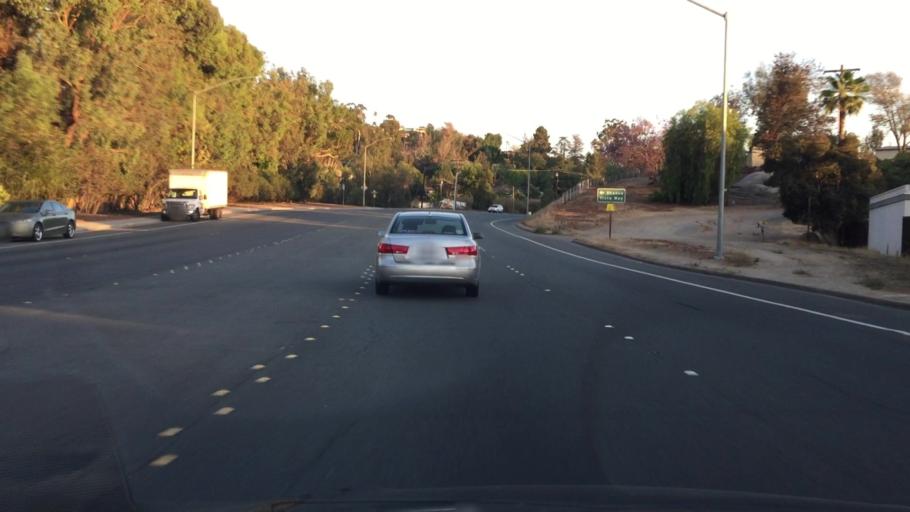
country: US
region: California
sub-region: San Diego County
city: Bostonia
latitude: 32.7819
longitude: -116.9279
